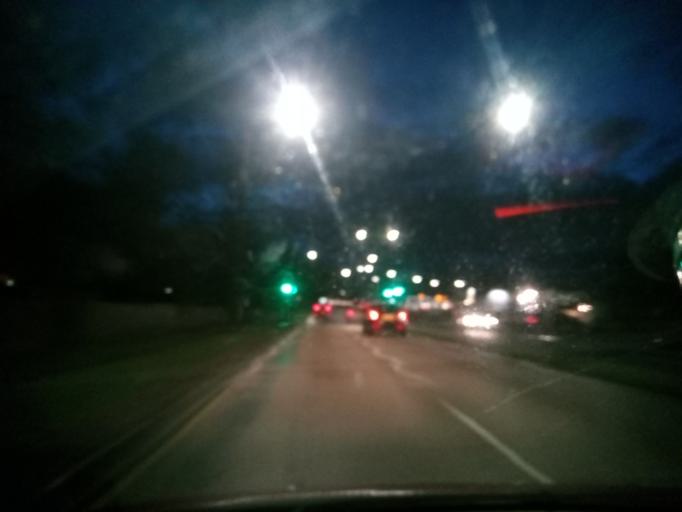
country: GB
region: England
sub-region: Doncaster
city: Bentley
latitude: 53.5005
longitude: -1.1680
